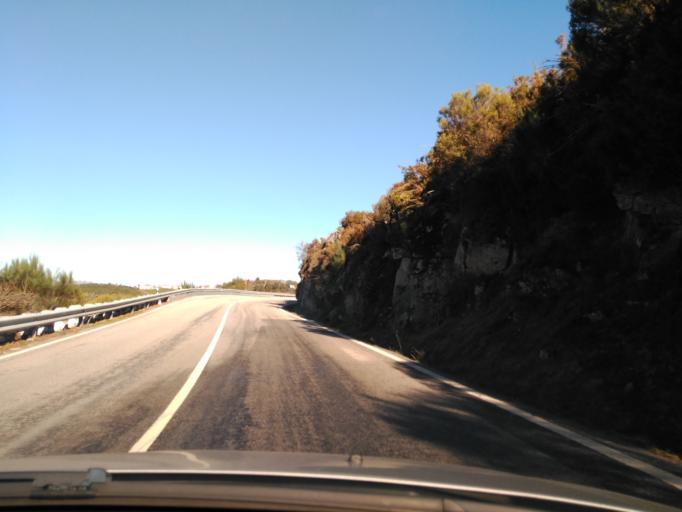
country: PT
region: Braga
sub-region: Vieira do Minho
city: Vieira do Minho
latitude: 41.6815
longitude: -7.9987
